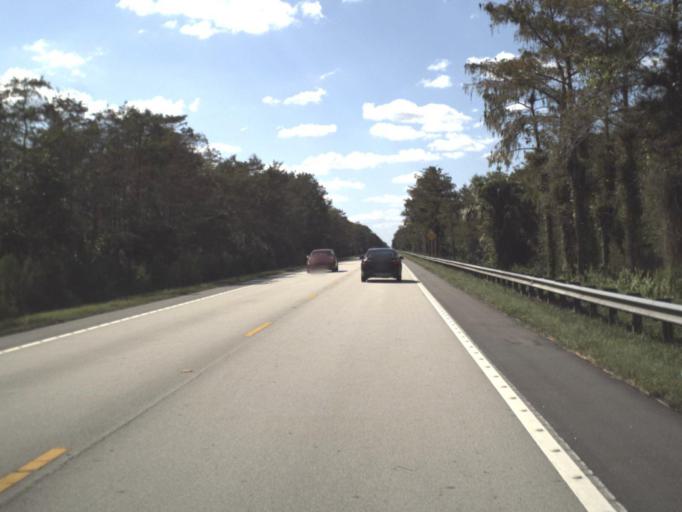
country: US
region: Florida
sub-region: Miami-Dade County
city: Kendall West
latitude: 25.8530
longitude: -80.9951
